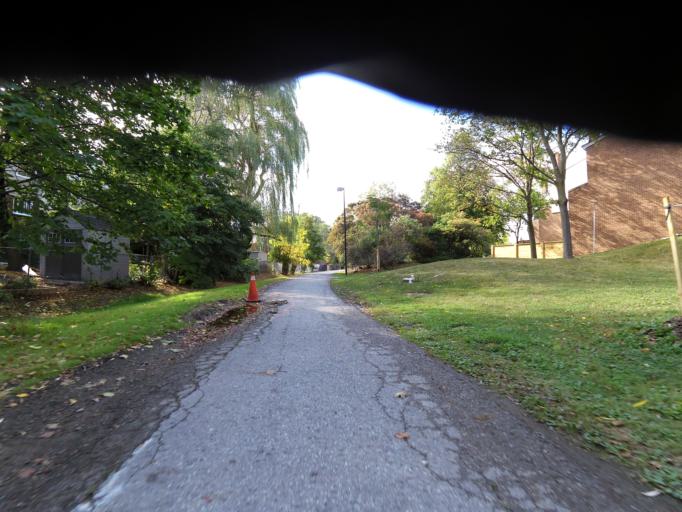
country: CA
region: Ontario
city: Mississauga
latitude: 43.5396
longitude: -79.6917
